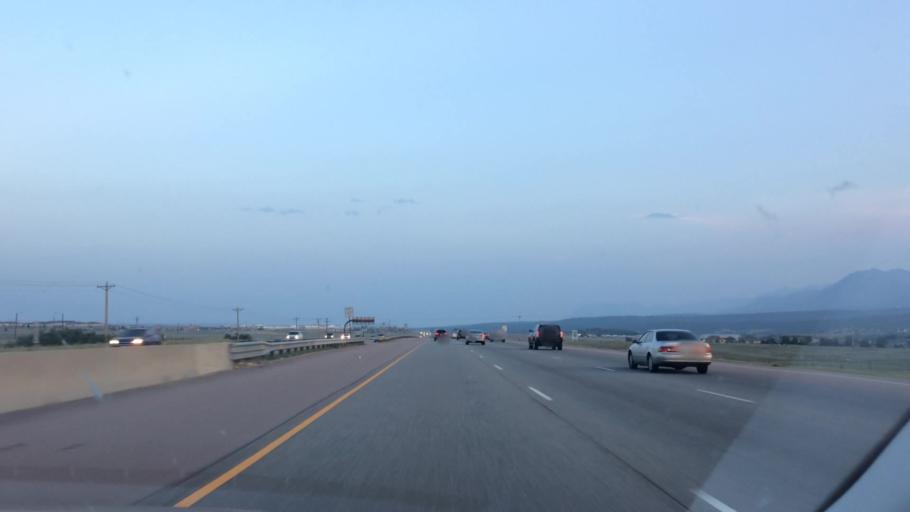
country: US
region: Colorado
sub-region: El Paso County
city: Monument
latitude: 39.0816
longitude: -104.8602
